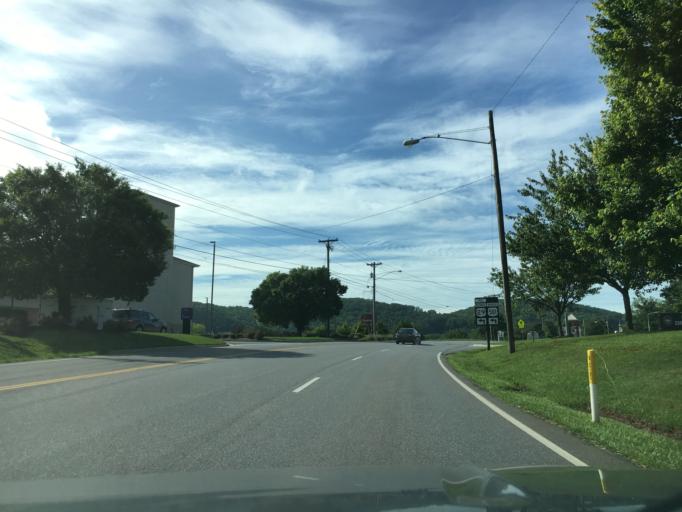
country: US
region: Virginia
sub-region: City of Lynchburg
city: West Lynchburg
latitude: 37.3643
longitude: -79.1717
